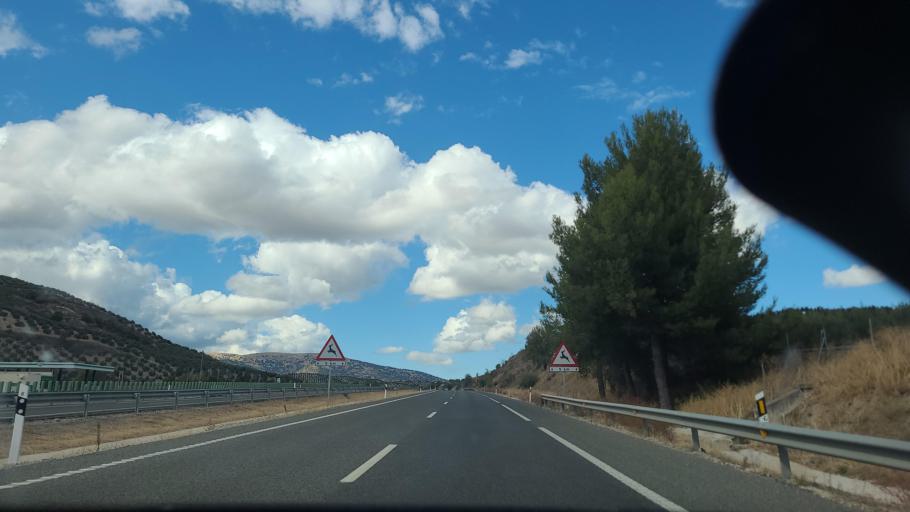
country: ES
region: Andalusia
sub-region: Provincia de Granada
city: Campotejar
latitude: 37.5042
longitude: -3.6300
